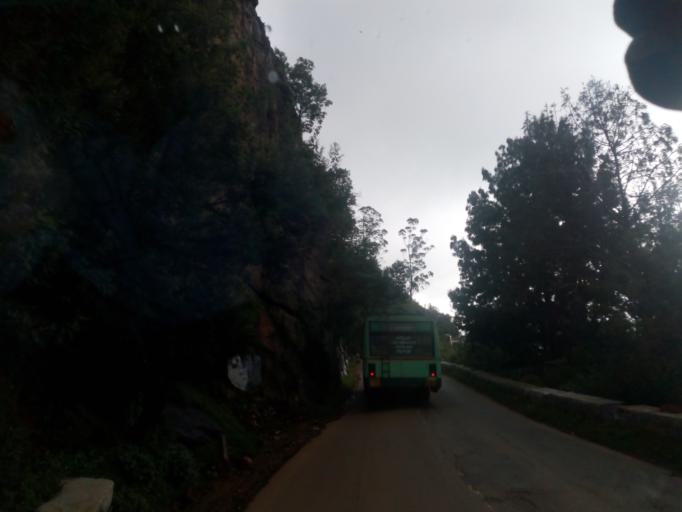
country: IN
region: Tamil Nadu
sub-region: Nilgiri
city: Ooty
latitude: 11.3894
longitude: 76.7205
